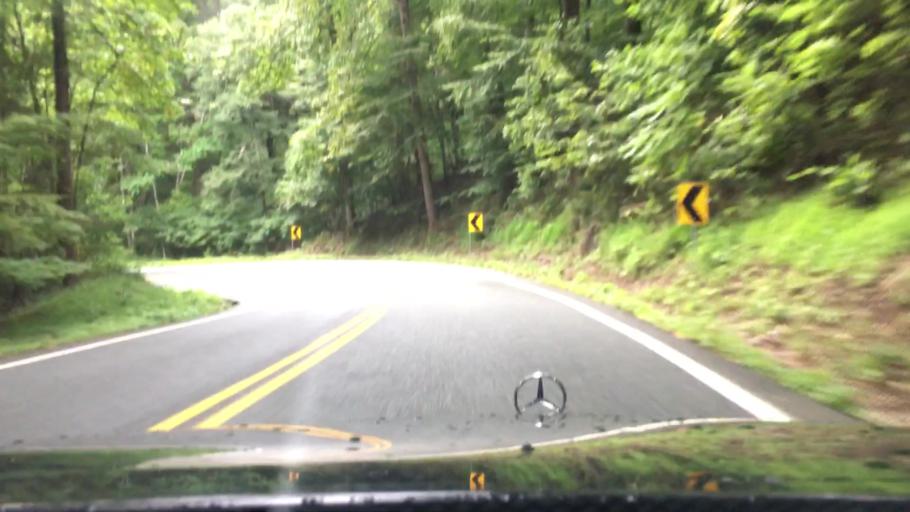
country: US
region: Virginia
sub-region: Nelson County
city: Nellysford
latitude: 37.8511
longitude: -78.9266
